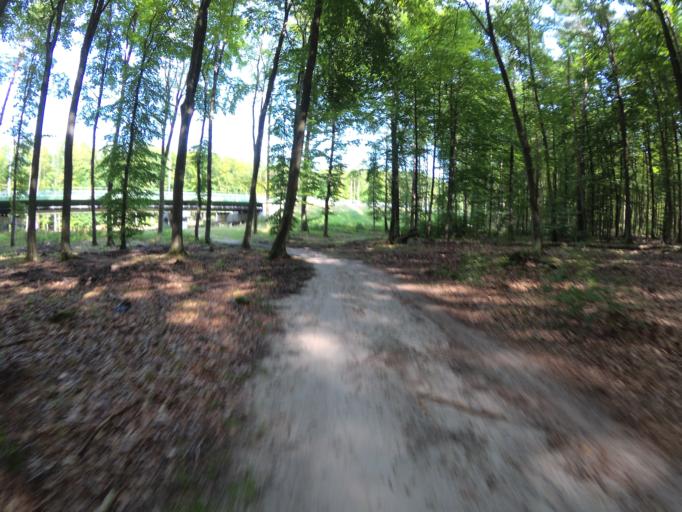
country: PL
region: Pomeranian Voivodeship
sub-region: Gdynia
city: Wielki Kack
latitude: 54.4984
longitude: 18.4833
